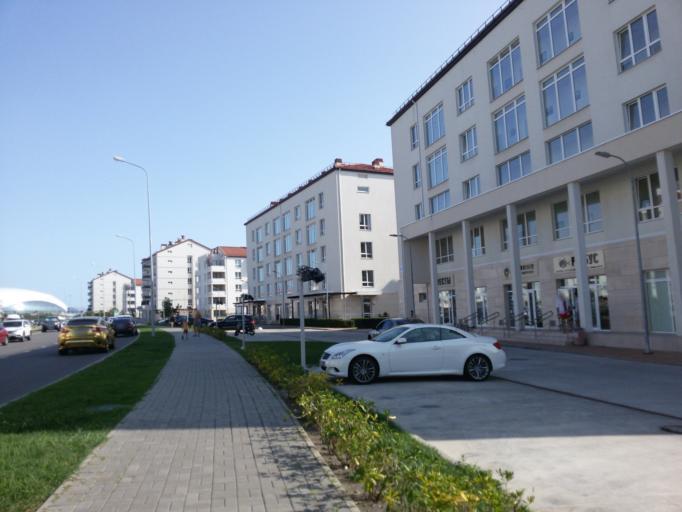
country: RU
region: Krasnodarskiy
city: Adler
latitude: 43.4086
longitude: 39.9397
